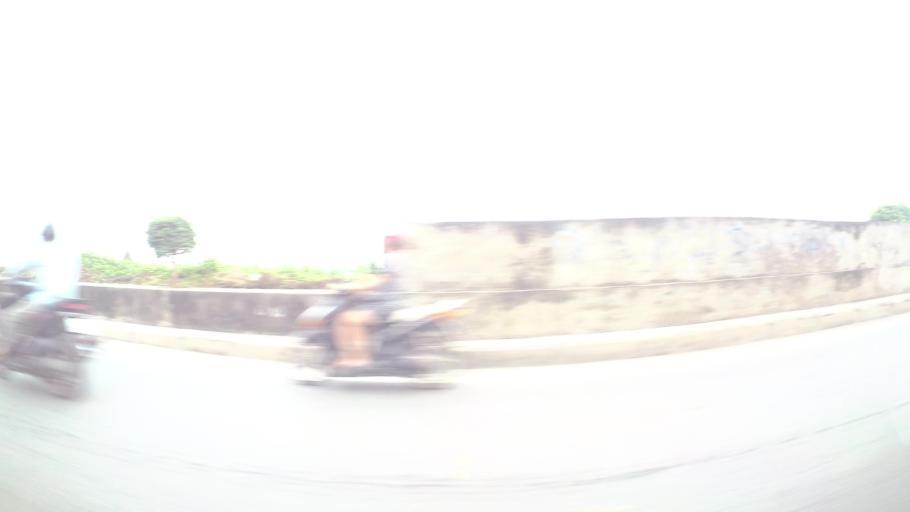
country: VN
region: Ha Noi
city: Hoan Kiem
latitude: 21.0673
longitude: 105.8734
